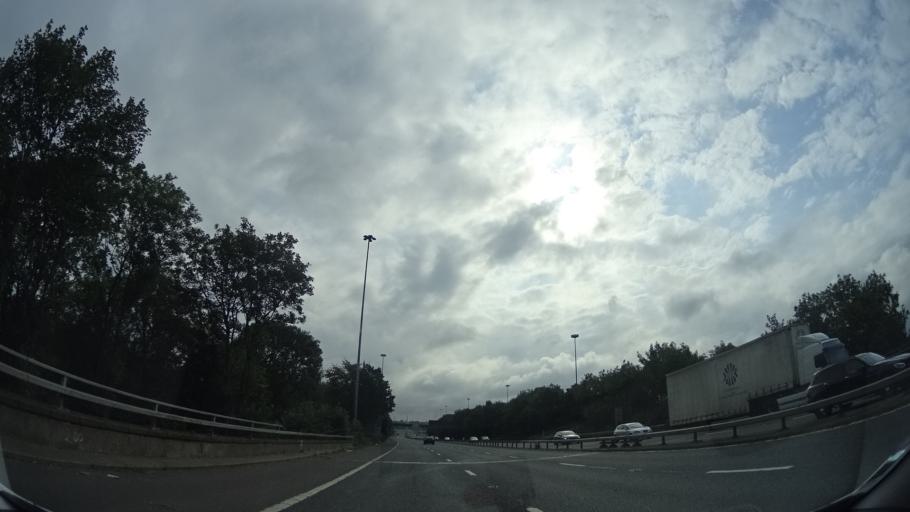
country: GB
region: England
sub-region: Knowsley
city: Huyton
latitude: 53.4064
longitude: -2.8907
